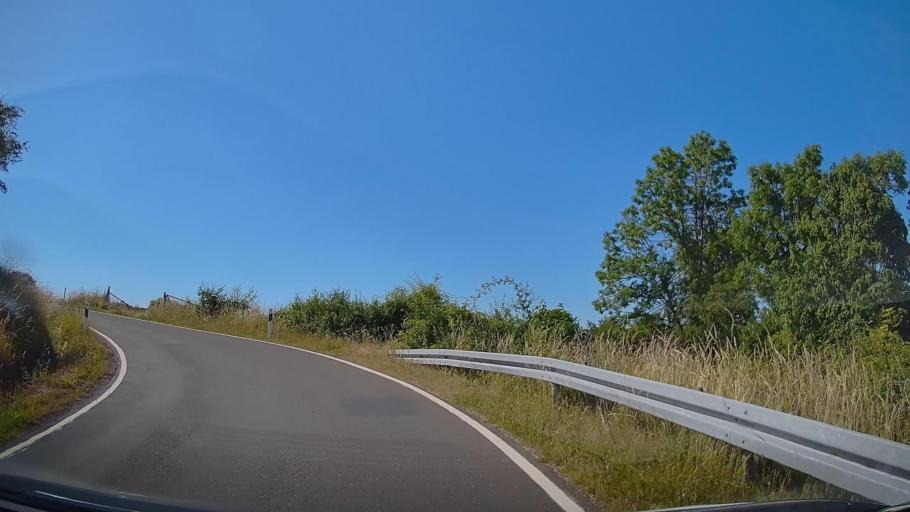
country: DE
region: Lower Saxony
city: Vahlbruch
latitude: 51.9757
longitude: 9.3551
